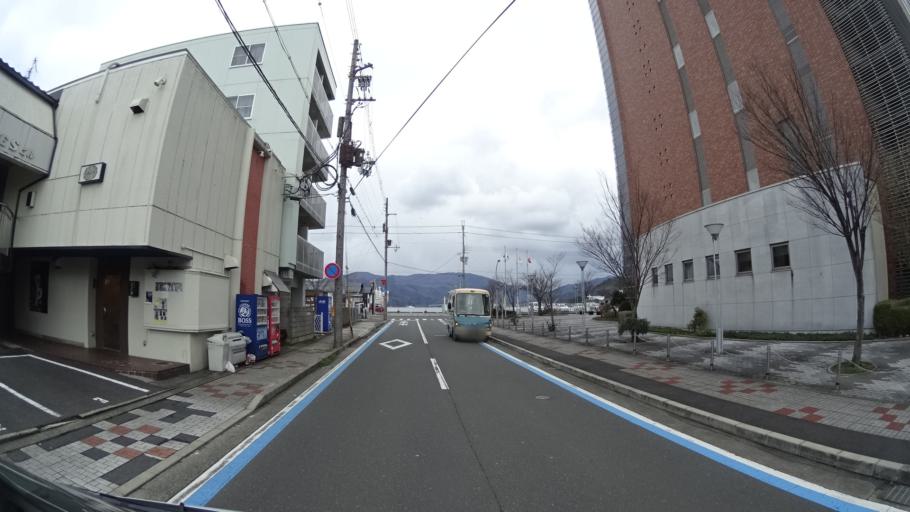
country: JP
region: Kyoto
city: Maizuru
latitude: 35.4766
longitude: 135.3948
